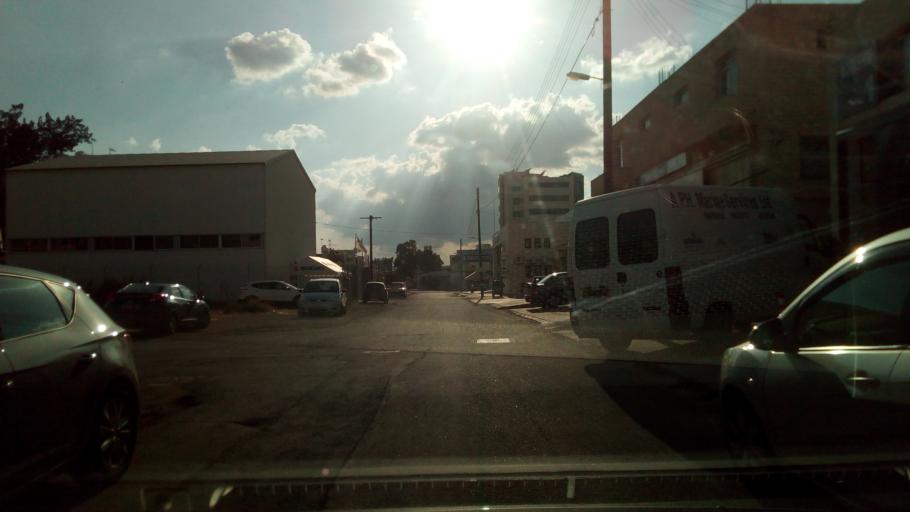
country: CY
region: Larnaka
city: Larnaca
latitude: 34.9298
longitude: 33.6310
